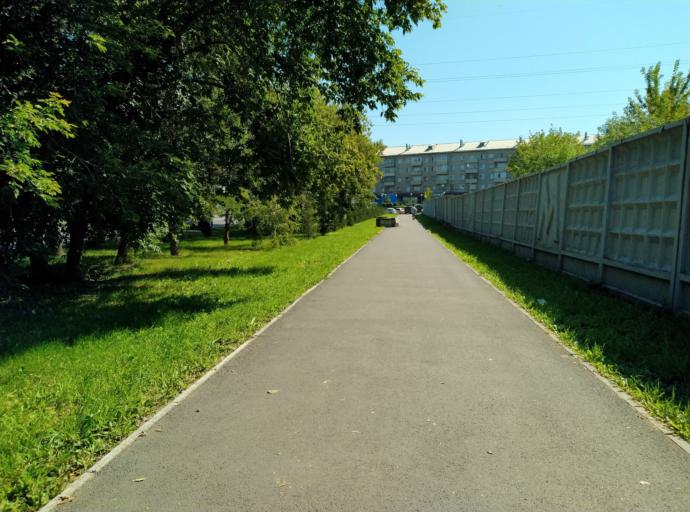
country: RU
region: Krasnoyarskiy
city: Krasnoyarsk
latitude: 56.0282
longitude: 92.7778
